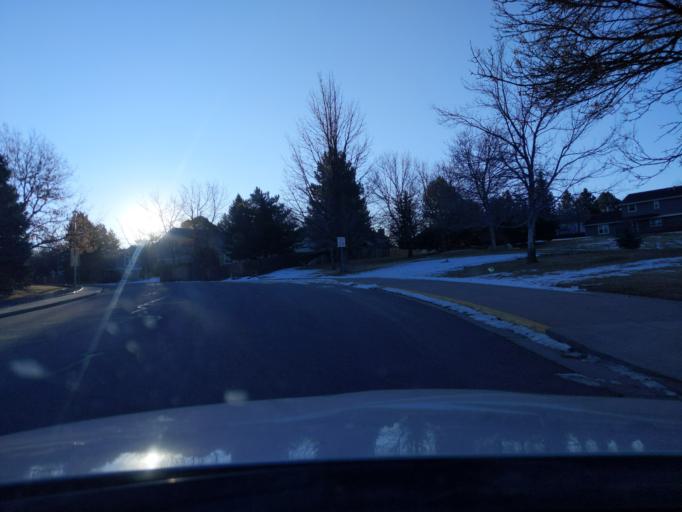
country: US
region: Colorado
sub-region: Arapahoe County
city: Centennial
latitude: 39.5742
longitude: -104.8876
